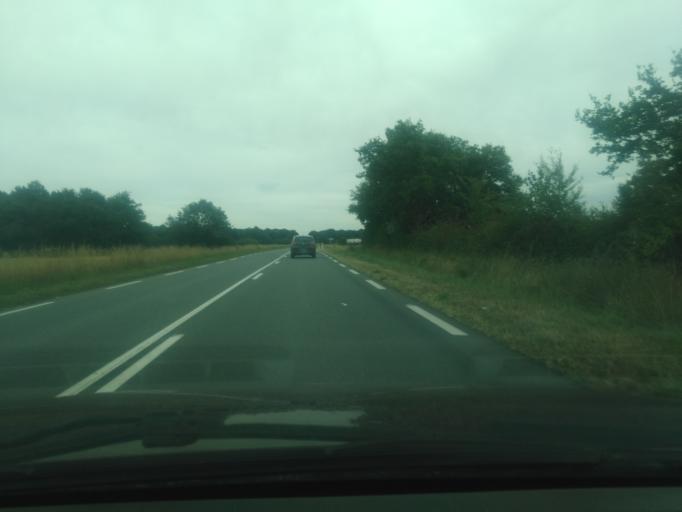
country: FR
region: Poitou-Charentes
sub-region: Departement de la Vienne
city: Chauvigny
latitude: 46.5716
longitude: 0.7317
